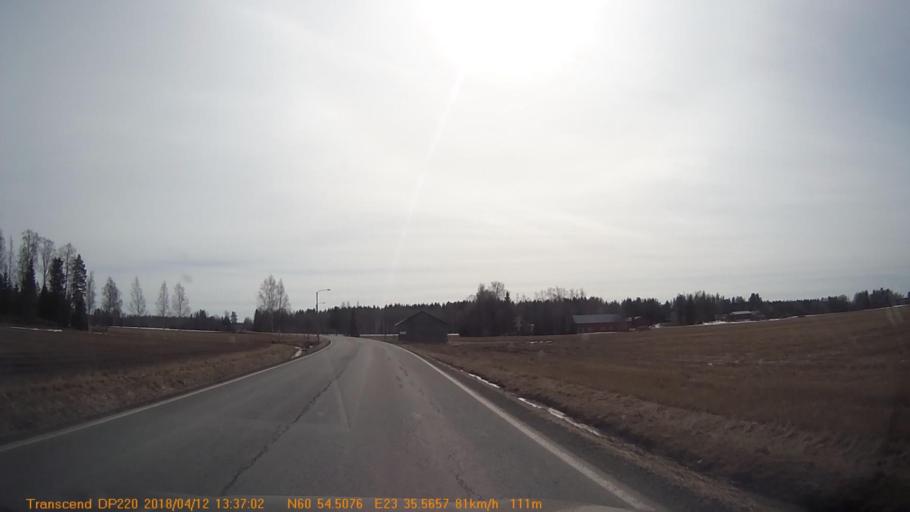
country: FI
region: Haeme
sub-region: Forssa
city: Forssa
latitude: 60.9082
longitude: 23.5927
